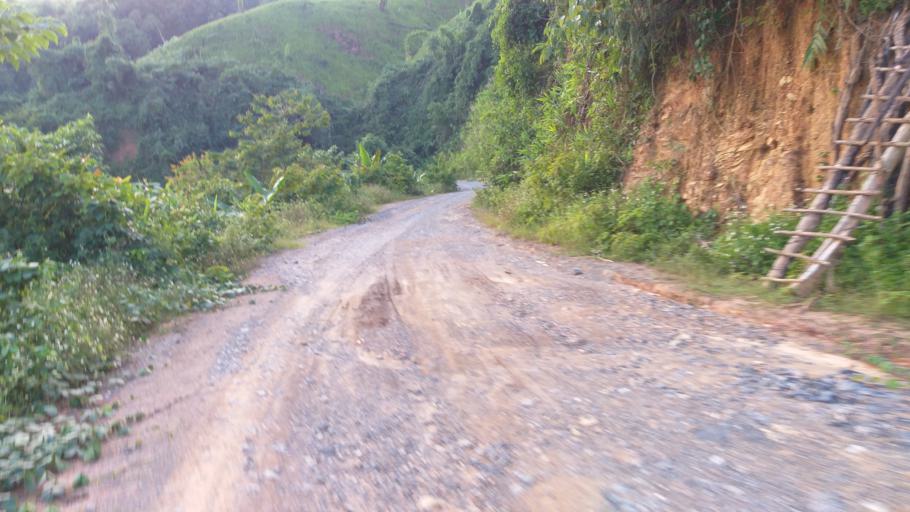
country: LA
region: Phongsali
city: Khoa
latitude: 21.1887
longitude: 102.5407
